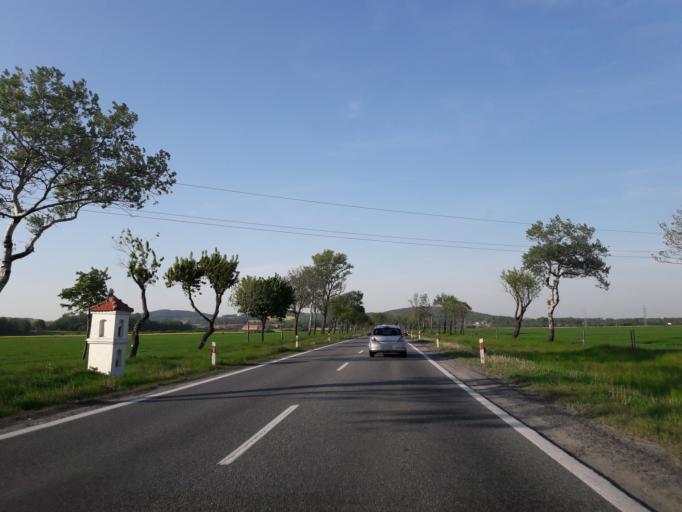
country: PL
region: Lower Silesian Voivodeship
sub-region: Powiat zabkowicki
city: Bardo
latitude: 50.5152
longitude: 16.7608
